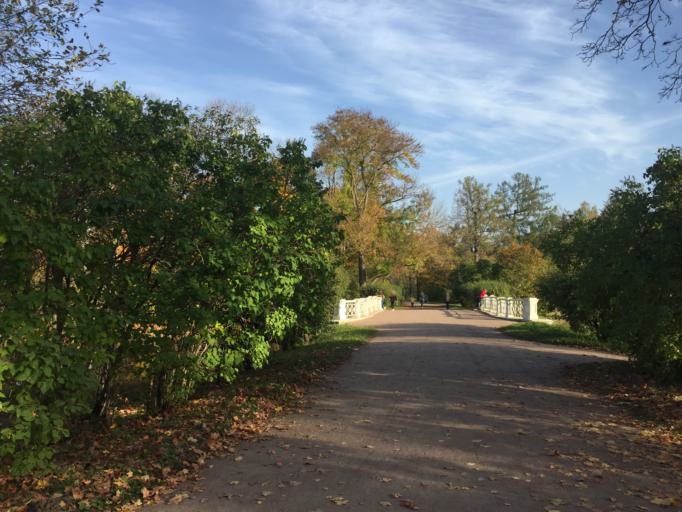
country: RU
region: St.-Petersburg
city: Pushkin
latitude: 59.7226
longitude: 30.3720
